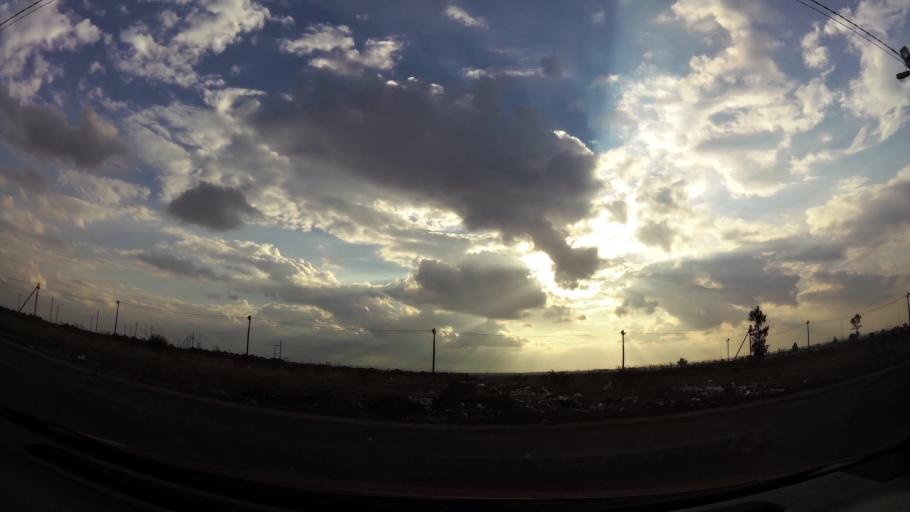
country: ZA
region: Gauteng
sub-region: Sedibeng District Municipality
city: Vanderbijlpark
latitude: -26.6082
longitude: 27.8118
